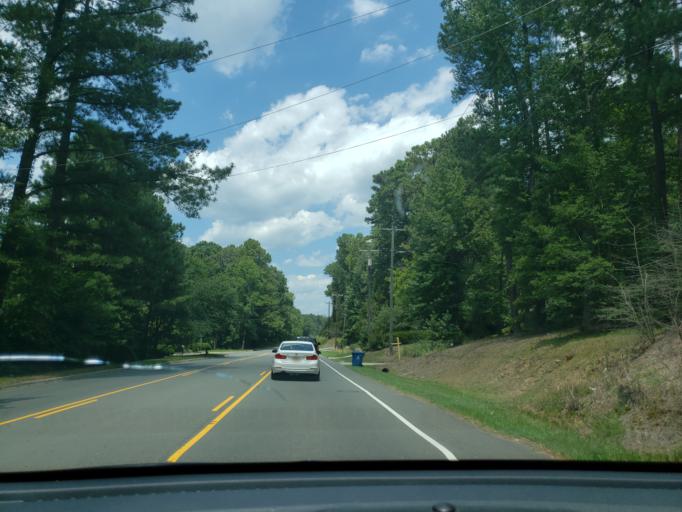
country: US
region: North Carolina
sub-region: Durham County
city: Durham
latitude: 35.9361
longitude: -78.9624
